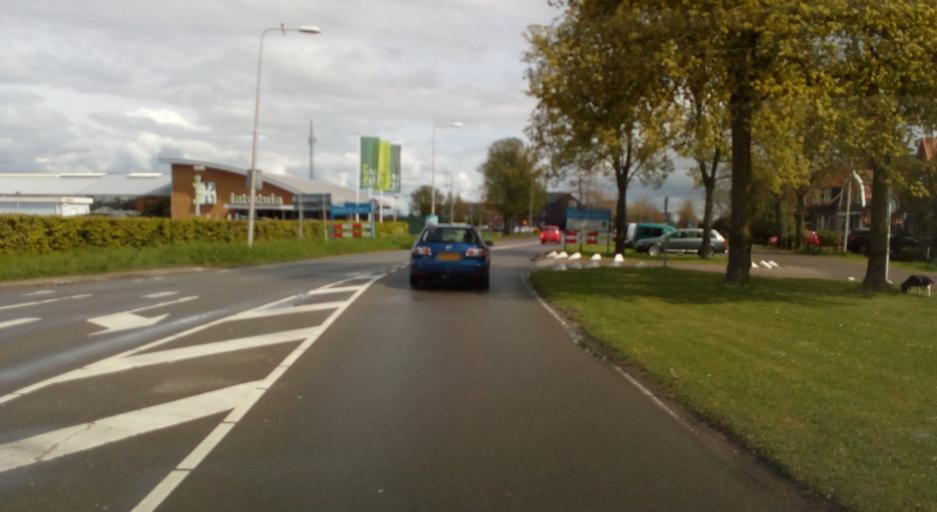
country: NL
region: South Holland
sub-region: Gemeente Zwijndrecht
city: Zwijndrecht
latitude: 51.8271
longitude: 4.6330
